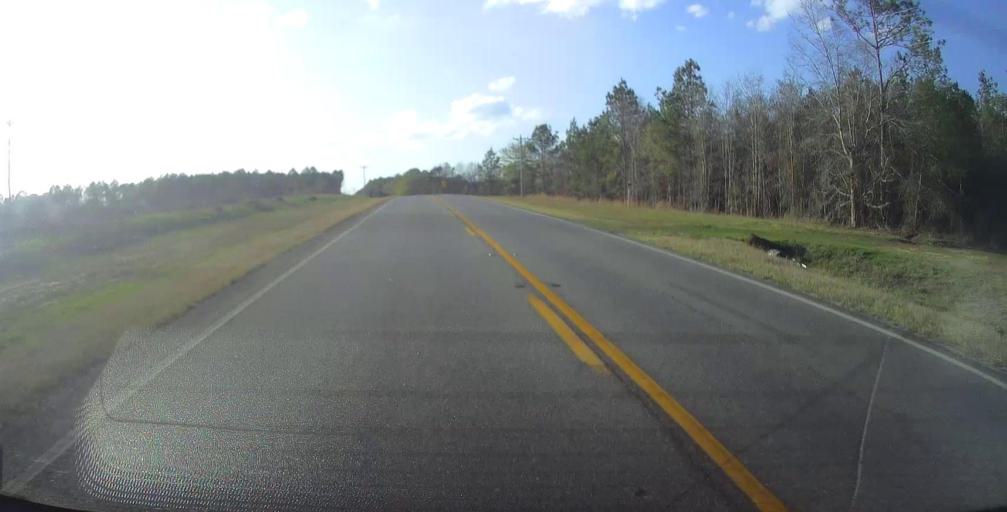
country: US
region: Georgia
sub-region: Tattnall County
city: Reidsville
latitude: 32.1342
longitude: -82.2255
